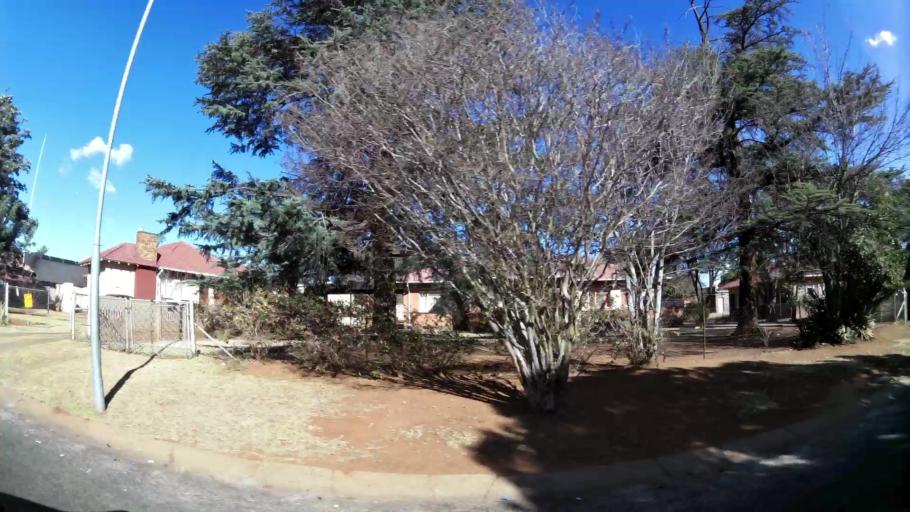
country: ZA
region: Gauteng
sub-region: West Rand District Municipality
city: Carletonville
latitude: -26.3718
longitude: 27.4026
